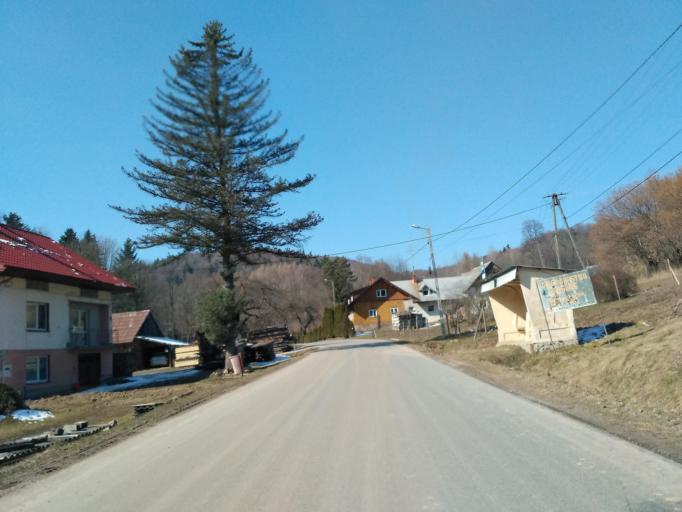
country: PL
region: Subcarpathian Voivodeship
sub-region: Powiat brzozowski
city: Jablonica Polska
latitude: 49.7549
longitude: 21.8753
